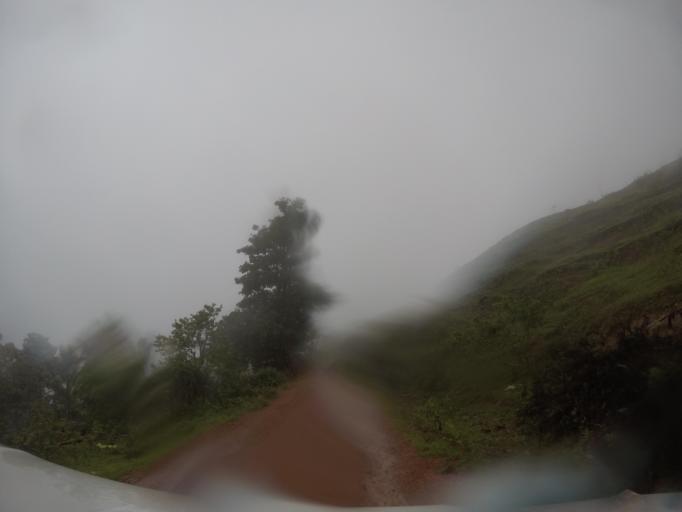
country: TL
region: Baucau
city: Venilale
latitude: -8.6388
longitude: 126.4171
